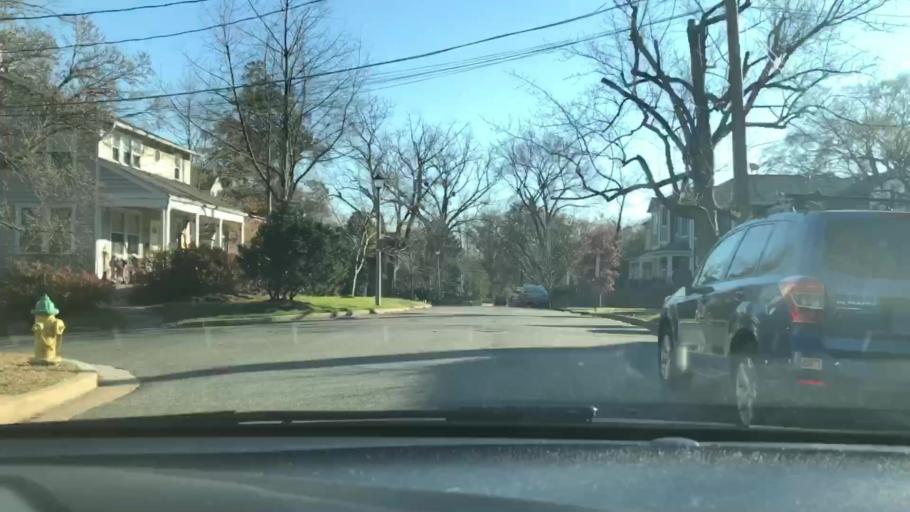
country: US
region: Virginia
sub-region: Arlington County
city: Arlington
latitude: 38.8788
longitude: -77.1017
